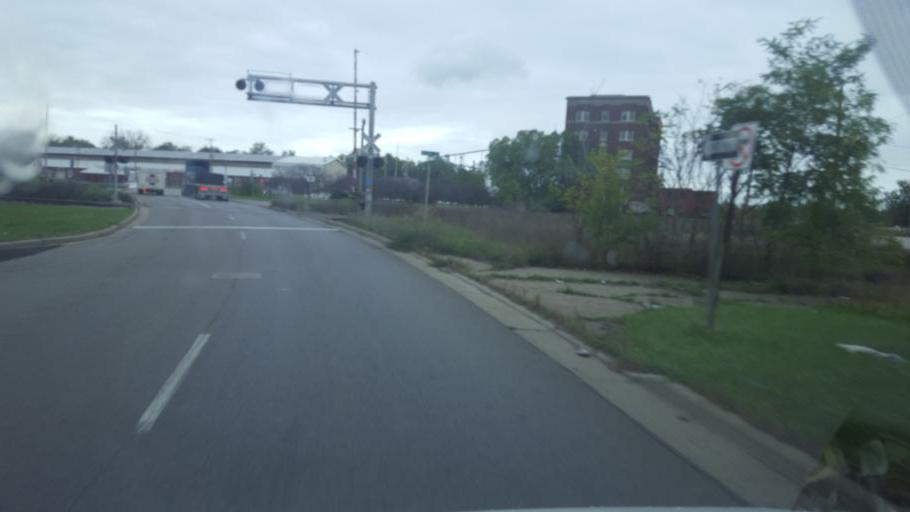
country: US
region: Ohio
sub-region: Richland County
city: Mansfield
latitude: 40.7671
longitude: -82.5137
